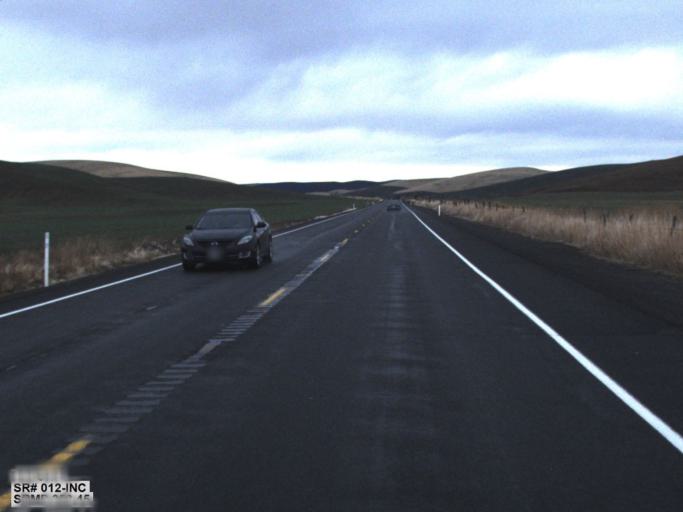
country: US
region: Washington
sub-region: Walla Walla County
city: Waitsburg
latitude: 46.2123
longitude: -118.1376
